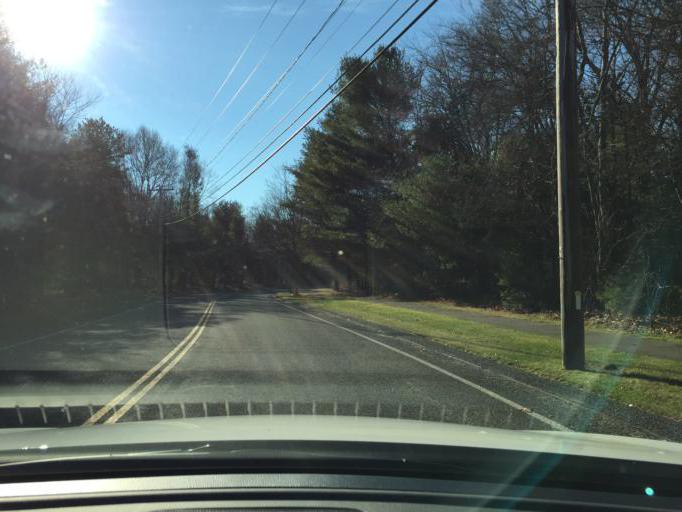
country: US
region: Massachusetts
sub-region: Bristol County
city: Mansfield
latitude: 42.0657
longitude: -71.2096
